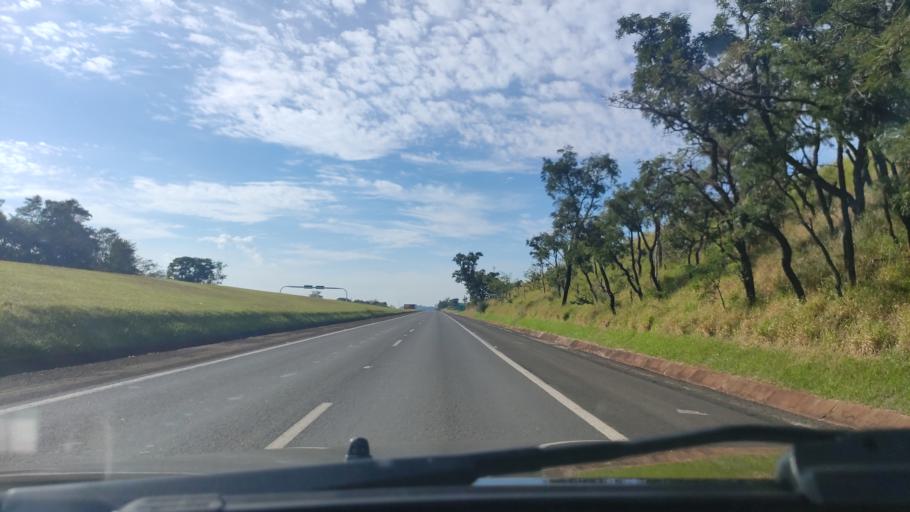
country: BR
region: Sao Paulo
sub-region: Avare
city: Avare
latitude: -22.9753
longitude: -48.7872
